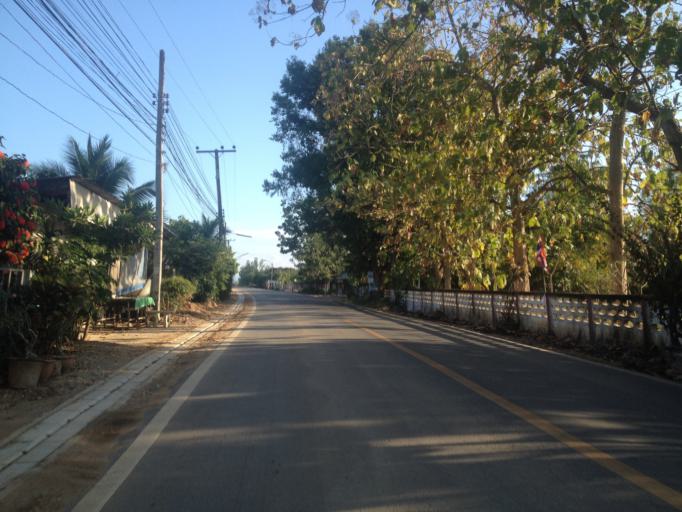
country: TH
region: Chiang Mai
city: San Pa Tong
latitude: 18.5882
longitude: 98.8624
